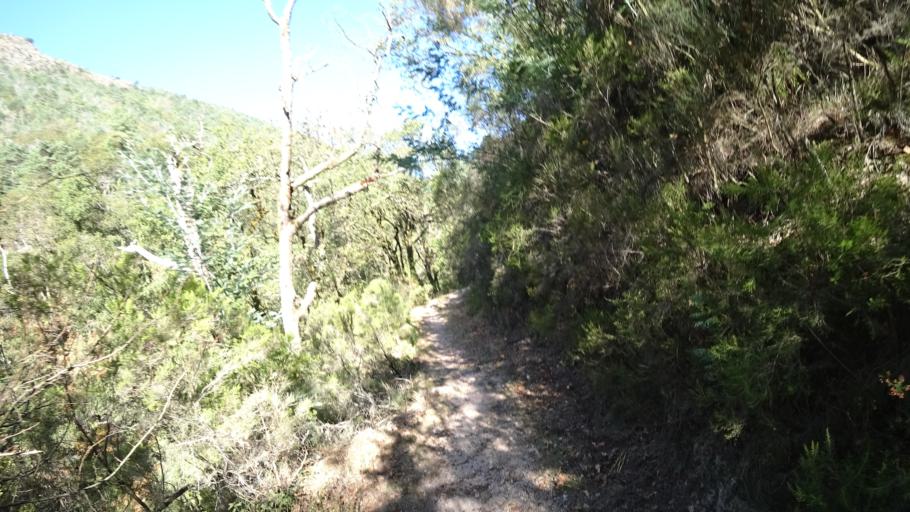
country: PT
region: Braga
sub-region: Vieira do Minho
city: Real
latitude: 41.7560
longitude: -8.1501
